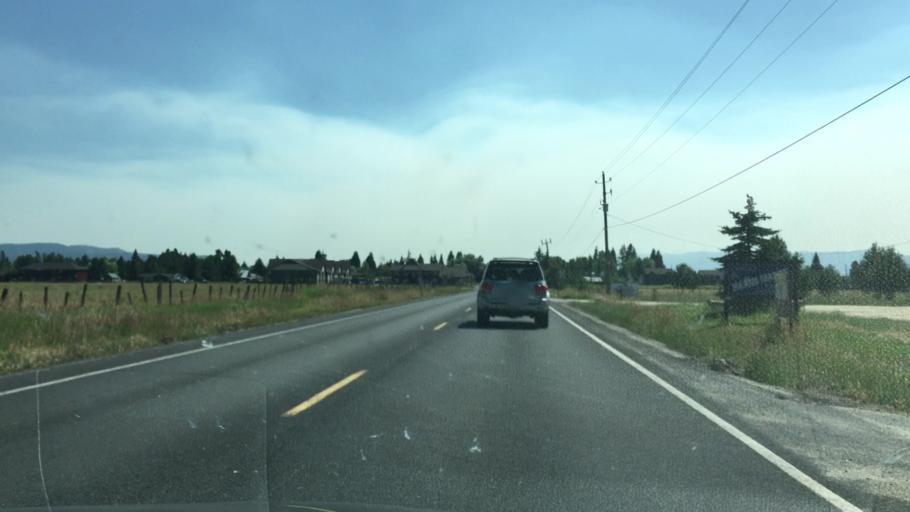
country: US
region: Idaho
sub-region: Valley County
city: McCall
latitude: 44.7378
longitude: -116.0783
